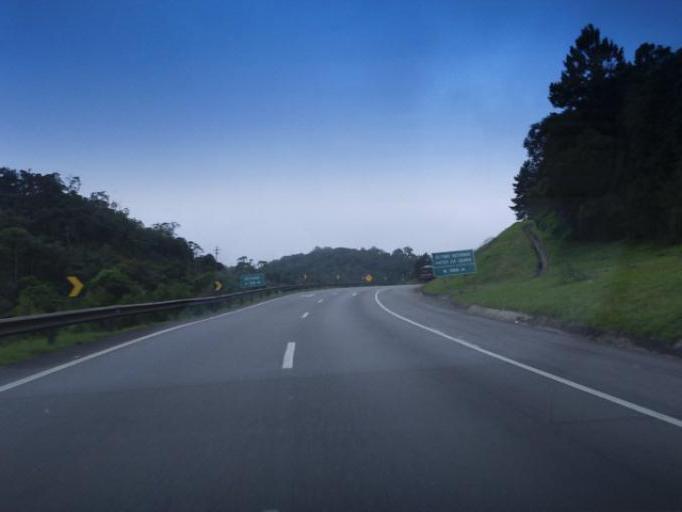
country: BR
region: Parana
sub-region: Sao Jose Dos Pinhais
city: Sao Jose dos Pinhais
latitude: -25.8536
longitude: -48.9923
